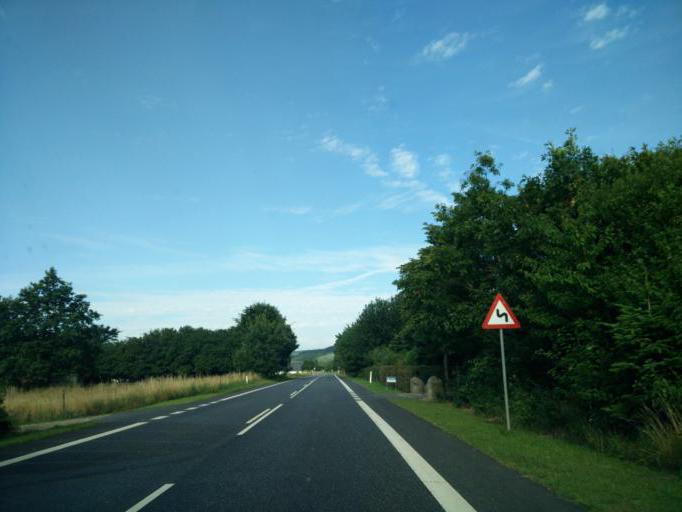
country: DK
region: Central Jutland
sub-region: Favrskov Kommune
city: Ulstrup
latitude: 56.3964
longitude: 9.7646
